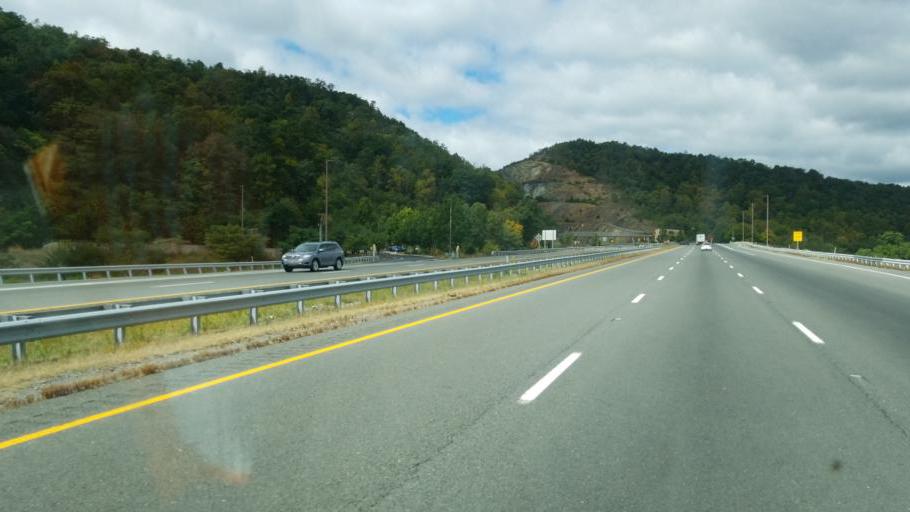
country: US
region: Maryland
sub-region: Washington County
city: Hancock
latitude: 39.7141
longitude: -78.2793
